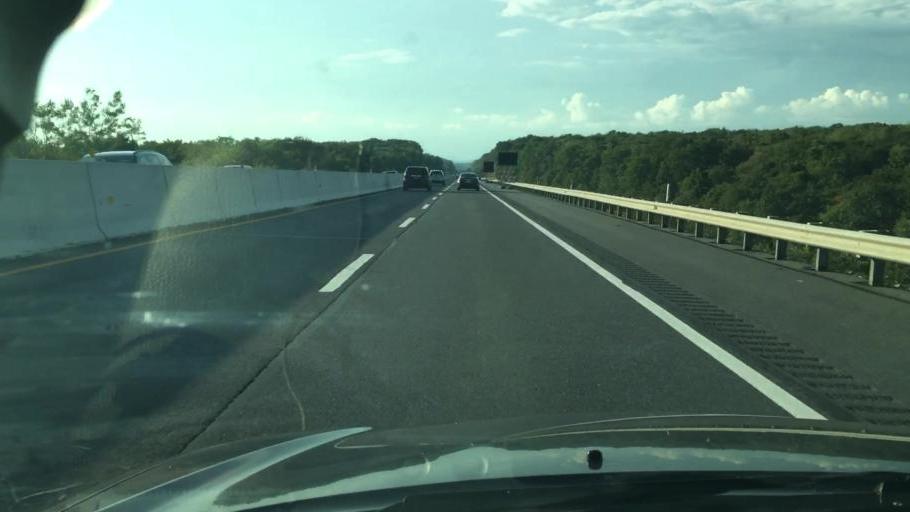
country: US
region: Pennsylvania
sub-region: Carbon County
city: Towamensing Trails
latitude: 41.0436
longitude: -75.6675
